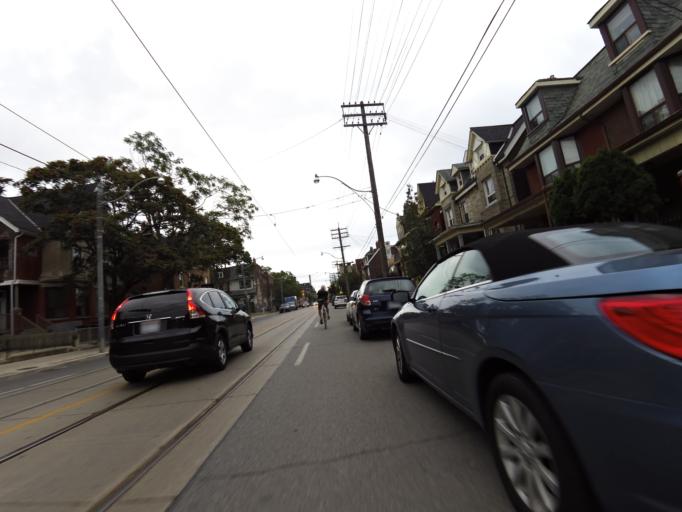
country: CA
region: Ontario
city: Toronto
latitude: 43.6503
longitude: -79.4156
